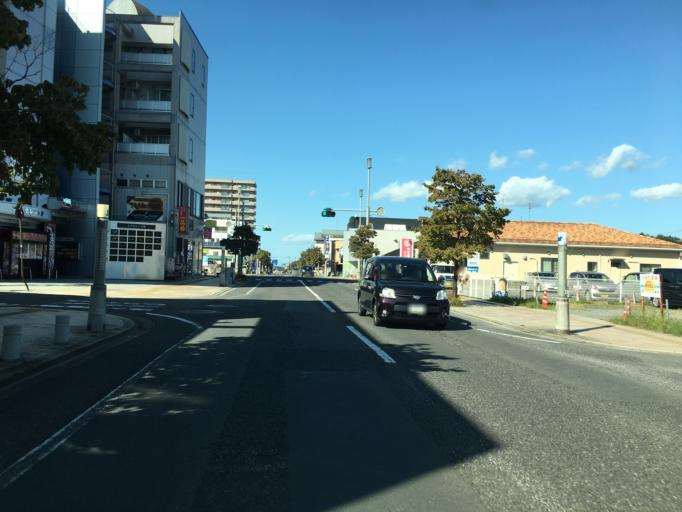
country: JP
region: Fukushima
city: Sukagawa
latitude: 37.2902
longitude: 140.3758
